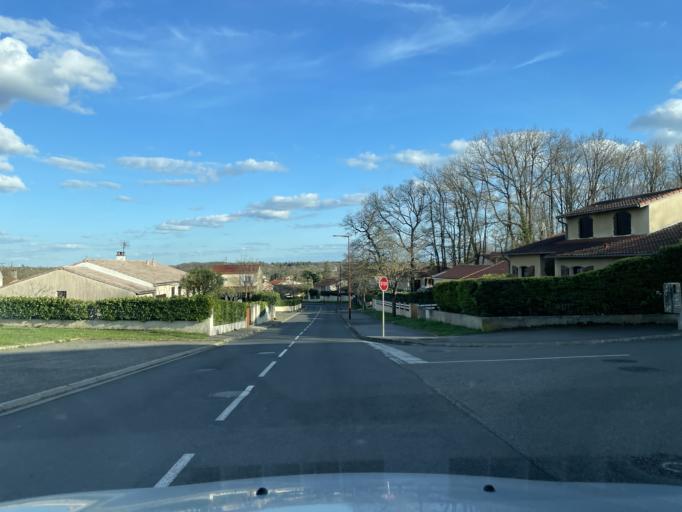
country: FR
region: Midi-Pyrenees
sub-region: Departement de la Haute-Garonne
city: Pibrac
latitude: 43.6149
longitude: 1.2789
